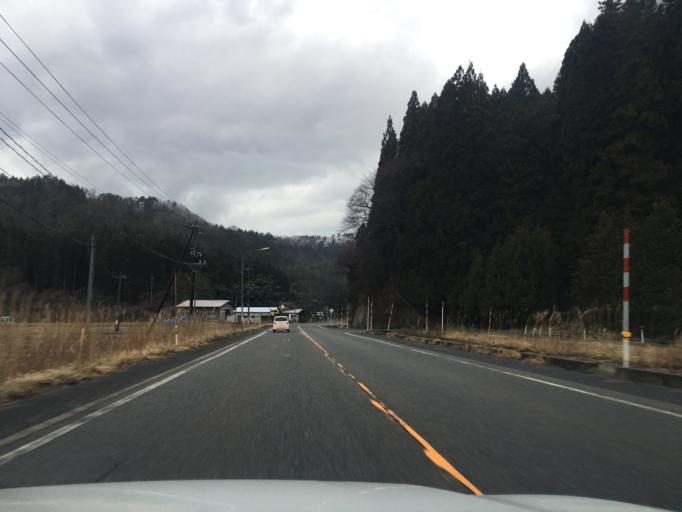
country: JP
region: Niigata
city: Murakami
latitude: 38.4668
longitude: 139.5601
